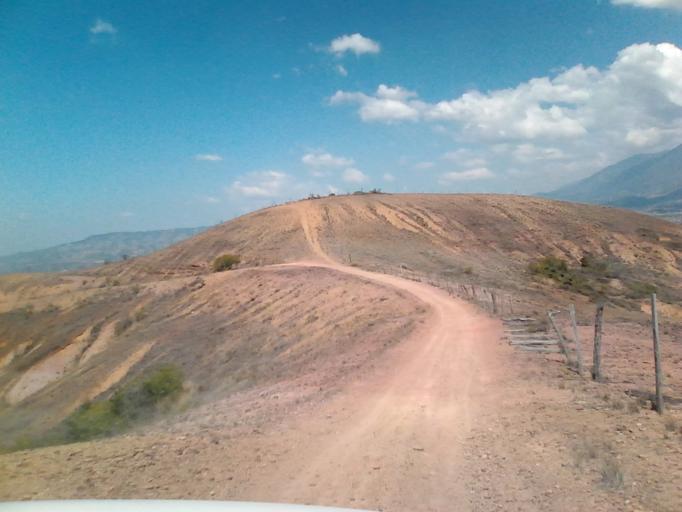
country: CO
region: Boyaca
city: Villa de Leiva
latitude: 5.6094
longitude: -73.5732
